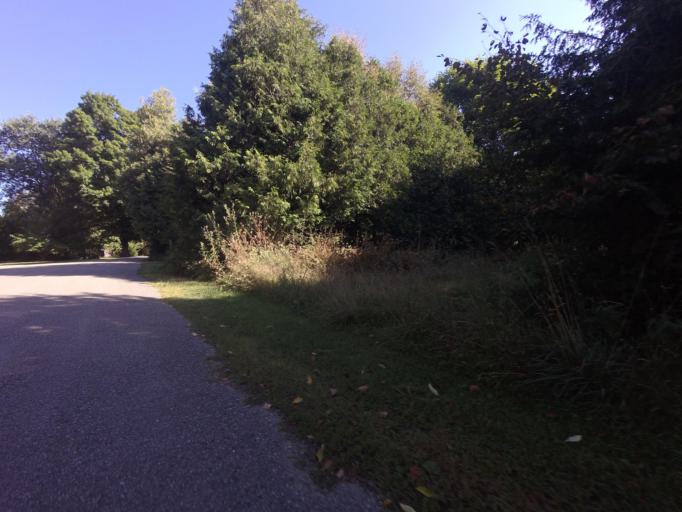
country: CA
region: Ontario
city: Waterloo
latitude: 43.6714
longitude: -80.4526
